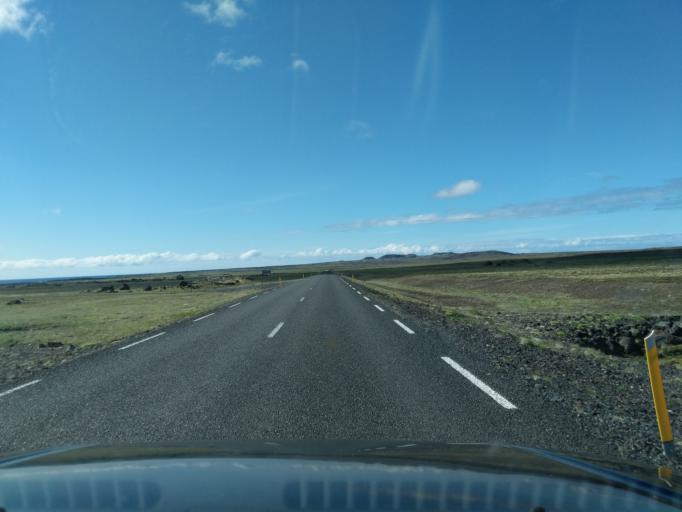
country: IS
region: West
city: Olafsvik
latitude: 64.8053
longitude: -23.9358
